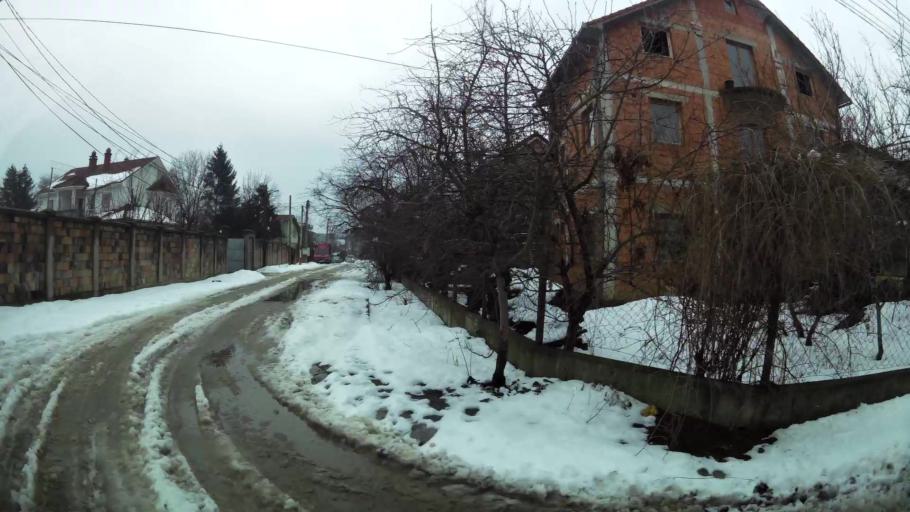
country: RS
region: Central Serbia
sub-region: Belgrade
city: Zemun
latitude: 44.8348
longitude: 20.3786
